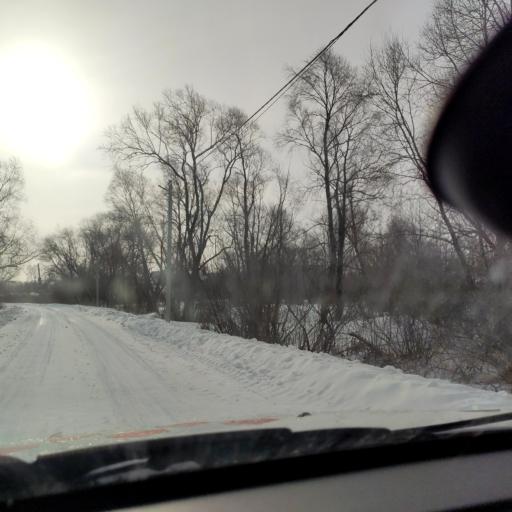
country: RU
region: Bashkortostan
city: Mikhaylovka
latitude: 54.8698
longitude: 55.7506
